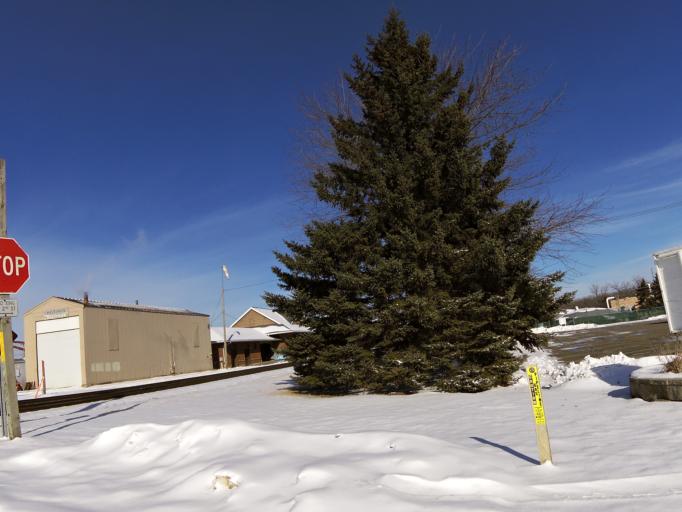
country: US
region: Minnesota
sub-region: Dakota County
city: Hastings
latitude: 44.7433
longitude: -92.8470
